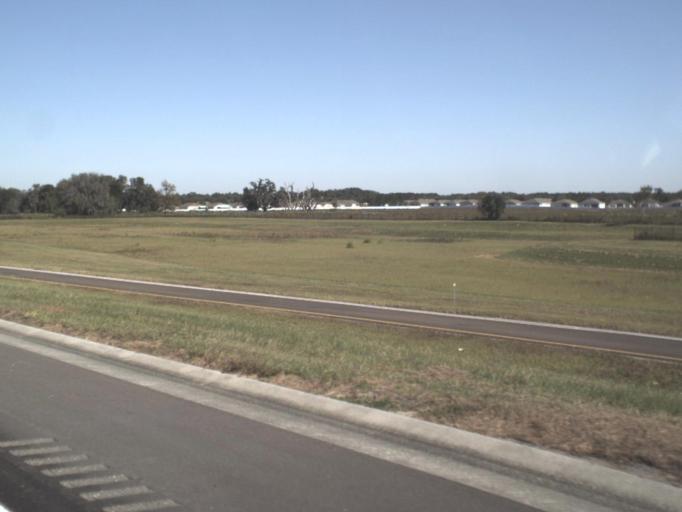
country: US
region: Florida
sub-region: Hernando County
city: Masaryktown
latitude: 28.4366
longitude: -82.4849
